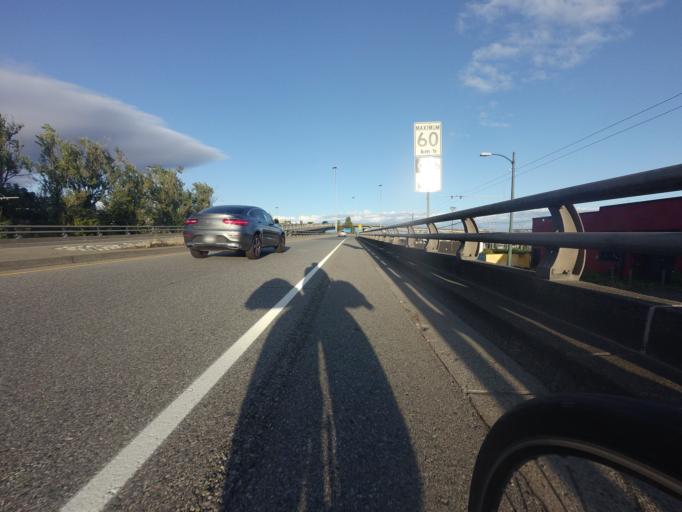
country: CA
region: British Columbia
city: Richmond
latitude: 49.2037
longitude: -123.1368
